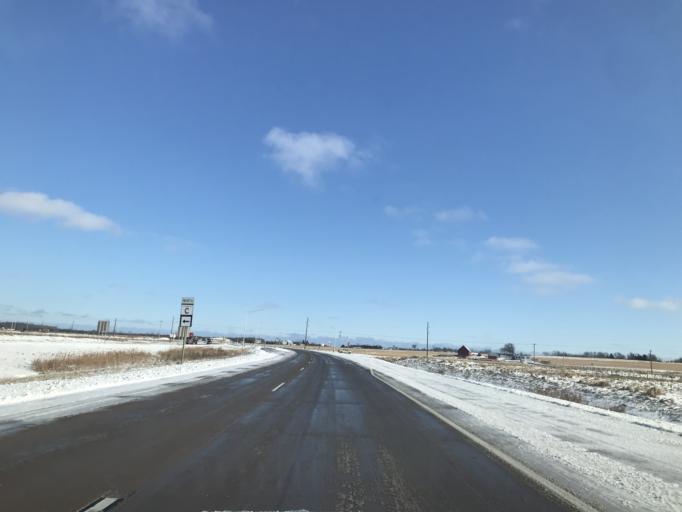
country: US
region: Wisconsin
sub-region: Kewaunee County
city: Luxemburg
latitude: 44.7164
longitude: -87.6239
